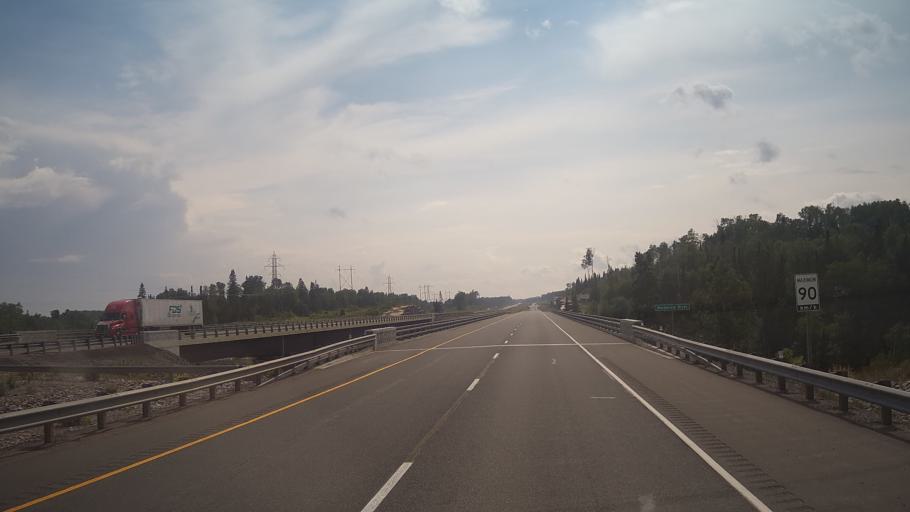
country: CA
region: Ontario
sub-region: Thunder Bay District
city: Thunder Bay
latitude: 48.5398
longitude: -88.9373
